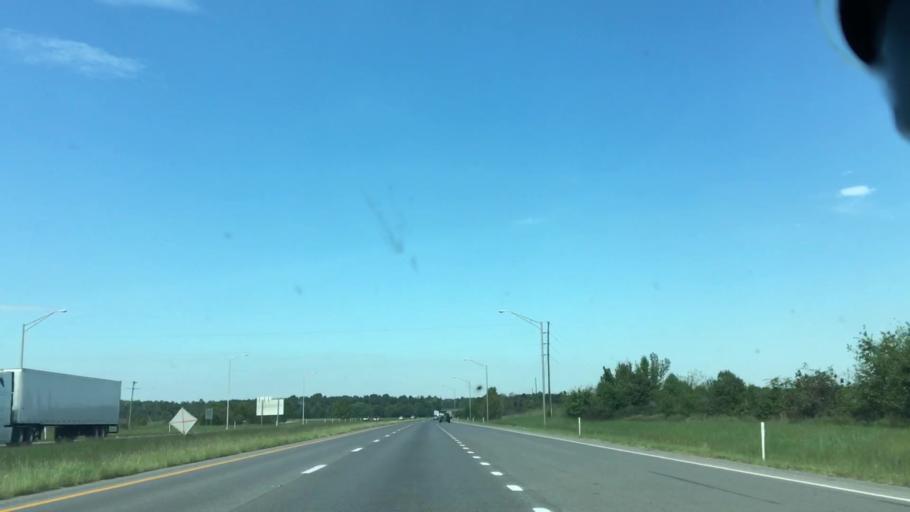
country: US
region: Kentucky
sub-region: Hopkins County
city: Madisonville
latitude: 37.2977
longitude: -87.4633
